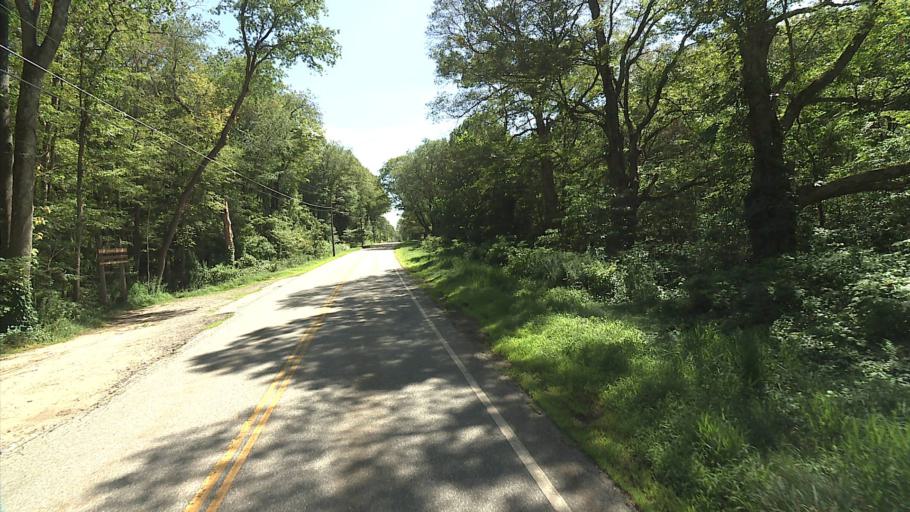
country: US
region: Connecticut
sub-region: Windham County
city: Windham
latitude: 41.7186
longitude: -72.0690
